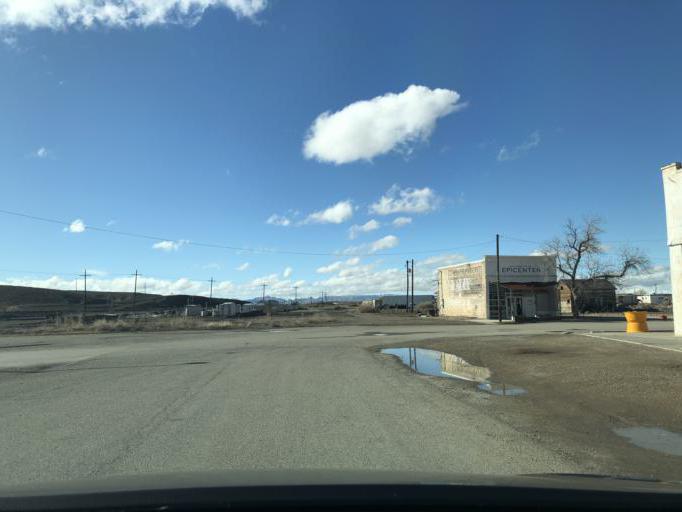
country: US
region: Utah
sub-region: Carbon County
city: East Carbon City
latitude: 38.9931
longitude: -110.1647
